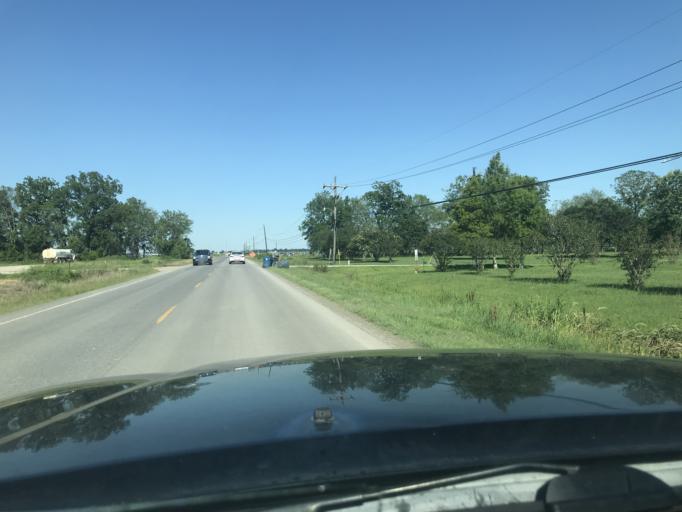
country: US
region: Louisiana
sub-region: West Baton Rouge Parish
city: Brusly
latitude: 30.4688
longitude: -91.3240
